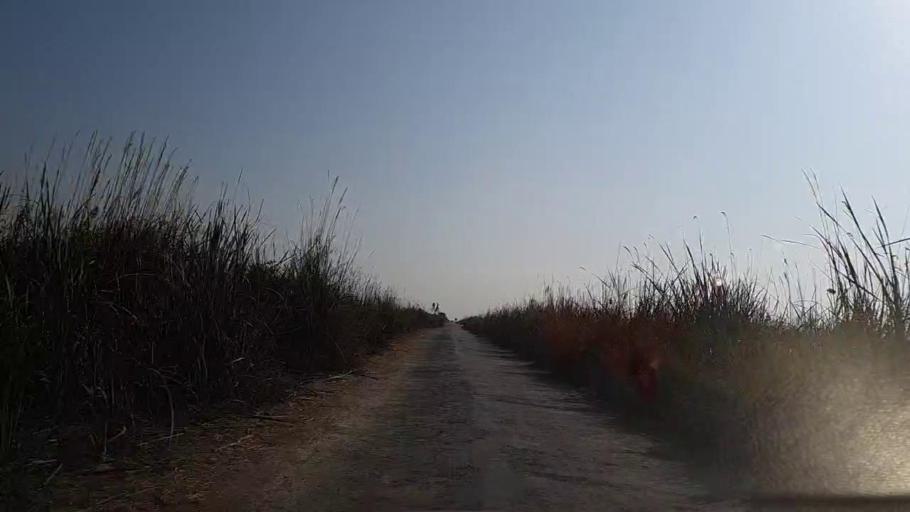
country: PK
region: Sindh
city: Tando Mittha Khan
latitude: 25.8935
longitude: 69.0769
